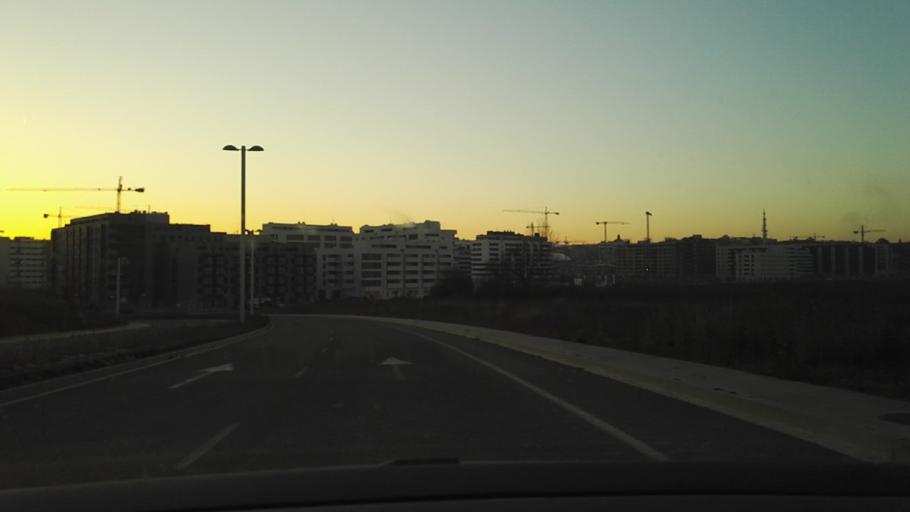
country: ES
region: Navarre
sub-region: Provincia de Navarra
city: Burlata
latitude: 42.8059
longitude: -1.6196
